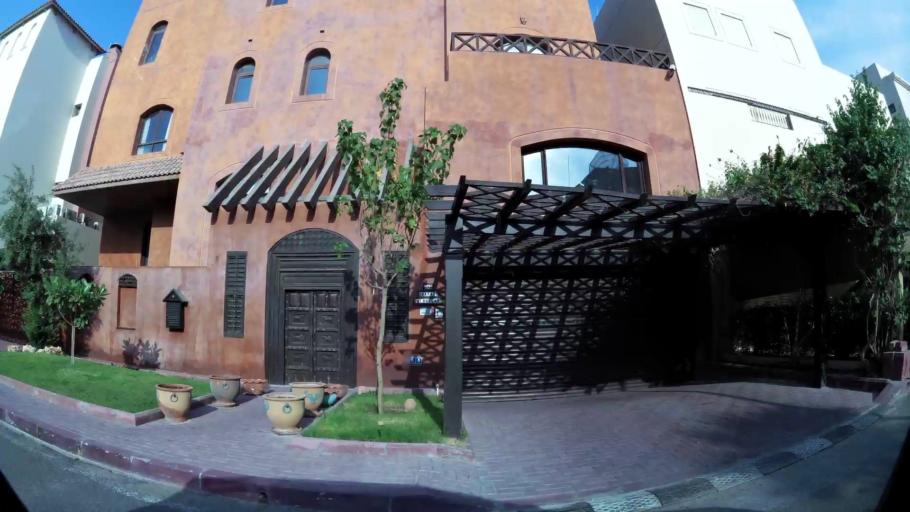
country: KW
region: Muhafazat Hawalli
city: Hawalli
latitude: 29.3208
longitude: 48.0049
